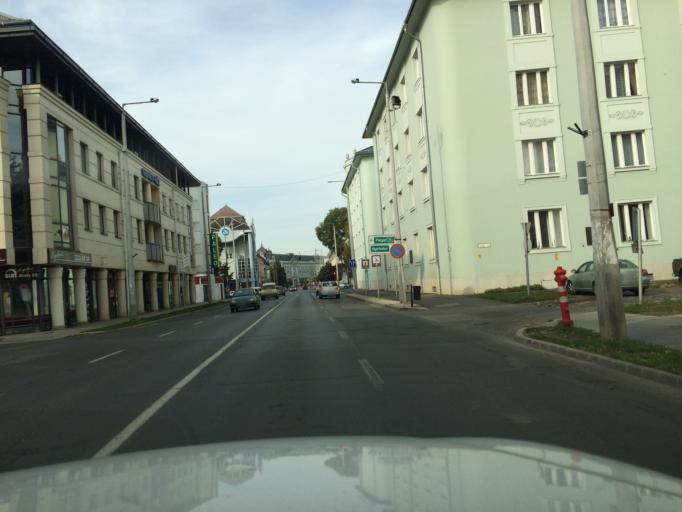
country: HU
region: Szabolcs-Szatmar-Bereg
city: Nyiregyhaza
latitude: 47.9530
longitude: 21.7181
